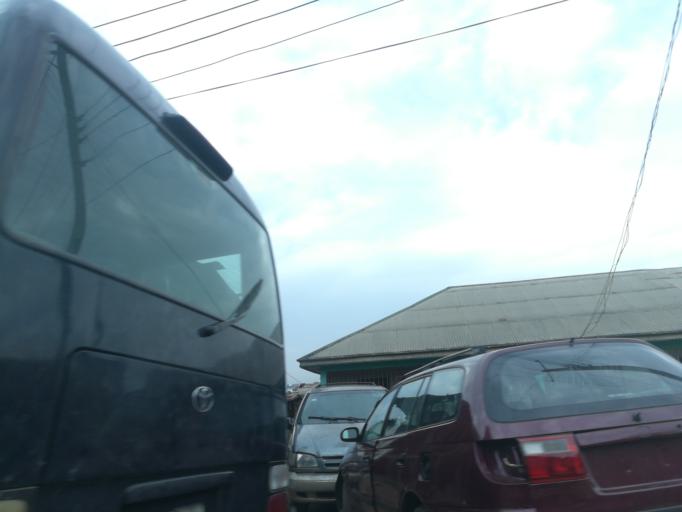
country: NG
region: Rivers
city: Port Harcourt
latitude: 4.8140
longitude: 6.9514
